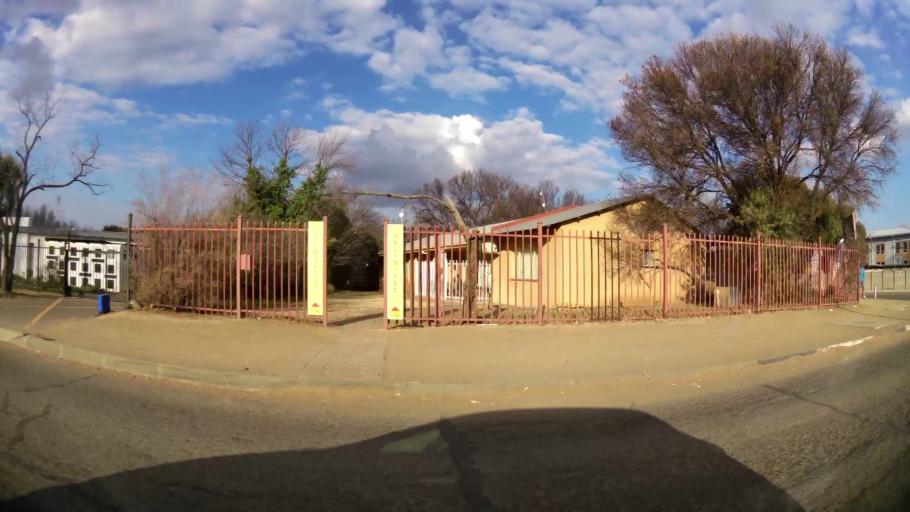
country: ZA
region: Orange Free State
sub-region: Mangaung Metropolitan Municipality
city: Bloemfontein
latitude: -29.1041
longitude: 26.1937
